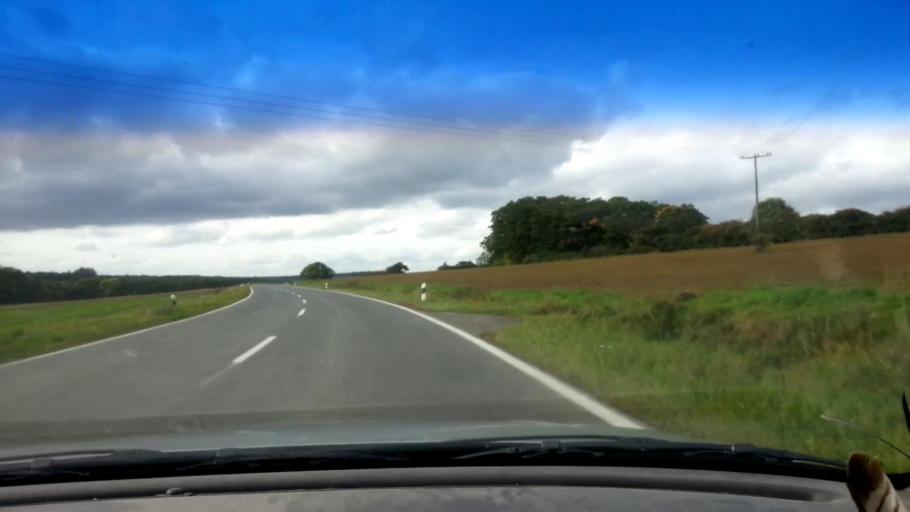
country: DE
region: Bavaria
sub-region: Upper Franconia
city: Schesslitz
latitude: 49.9831
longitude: 11.0196
